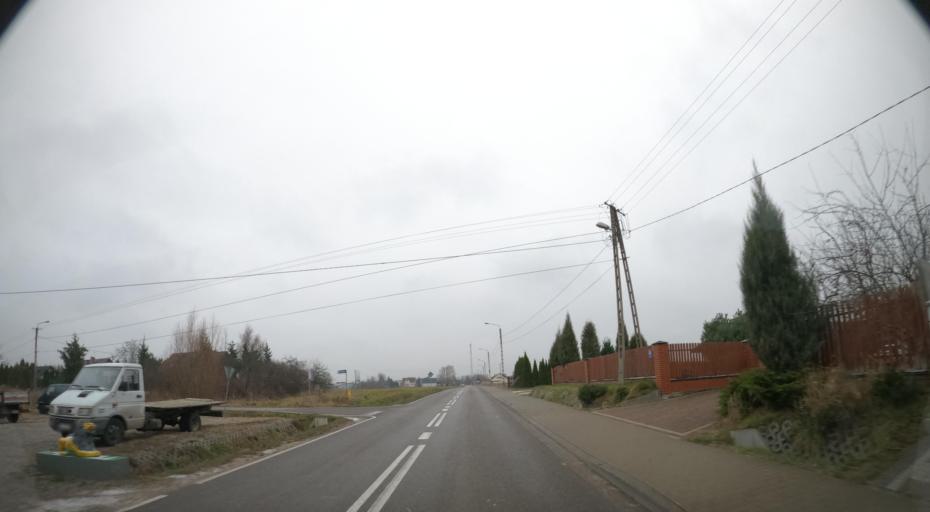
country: PL
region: Masovian Voivodeship
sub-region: Powiat radomski
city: Skaryszew
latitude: 51.3812
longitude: 21.2538
